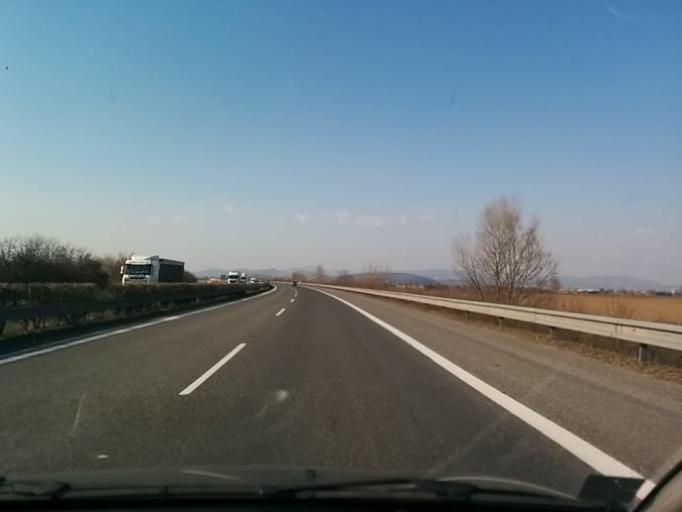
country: SK
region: Trenciansky
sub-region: Okres Nove Mesto nad Vahom
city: Nove Mesto nad Vahom
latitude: 48.7260
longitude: 17.8736
